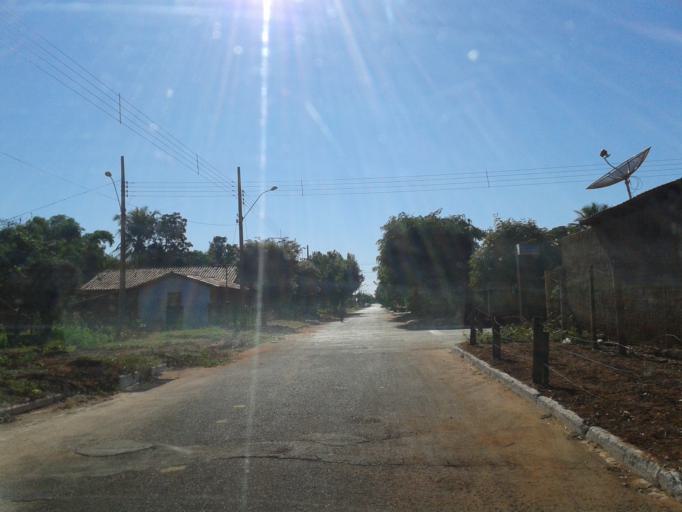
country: BR
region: Minas Gerais
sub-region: Santa Vitoria
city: Santa Vitoria
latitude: -18.8419
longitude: -50.1308
